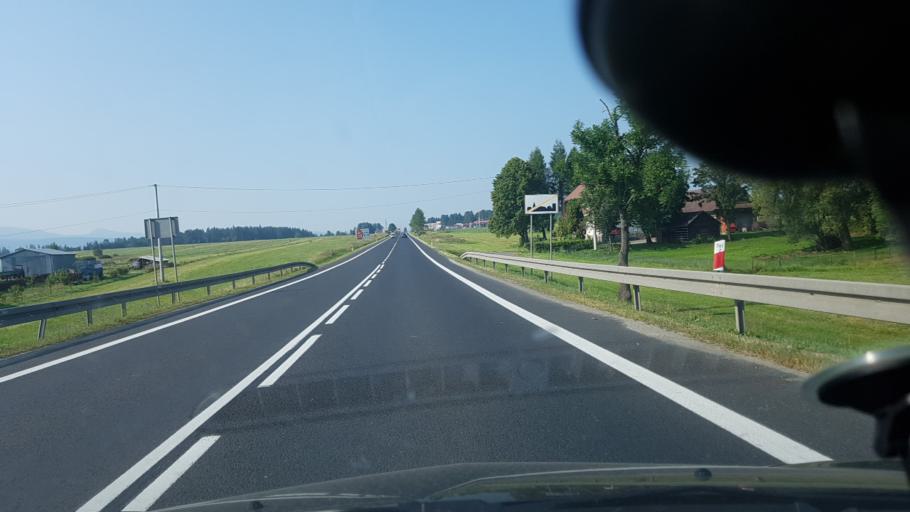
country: PL
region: Lesser Poland Voivodeship
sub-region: Powiat nowotarski
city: Chyzne
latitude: 49.4235
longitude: 19.6718
